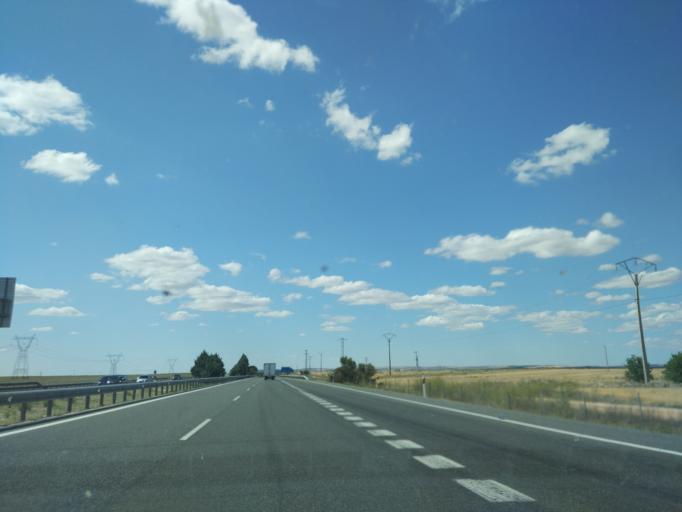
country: ES
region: Castille and Leon
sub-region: Provincia de Valladolid
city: San Vicente del Palacio
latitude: 41.2241
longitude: -4.8460
